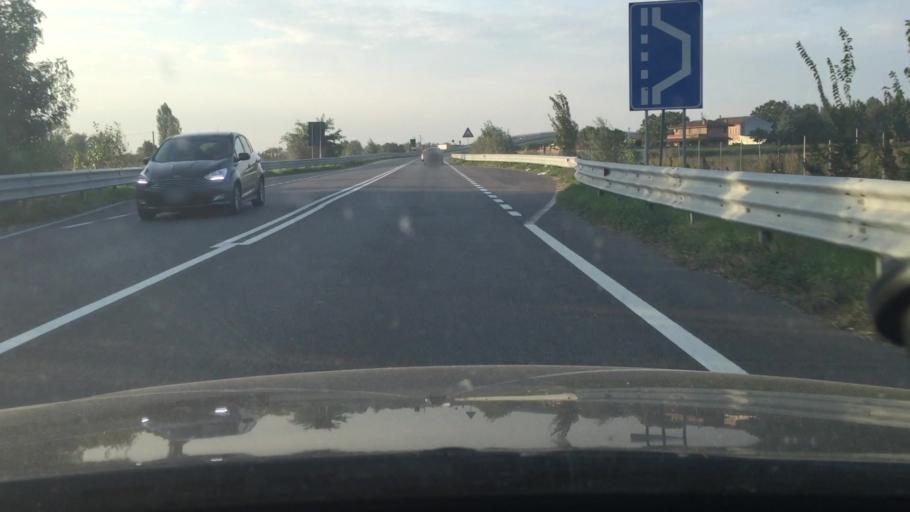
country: IT
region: Emilia-Romagna
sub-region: Provincia di Ferrara
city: Porotto-Cassama
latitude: 44.8357
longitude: 11.5753
